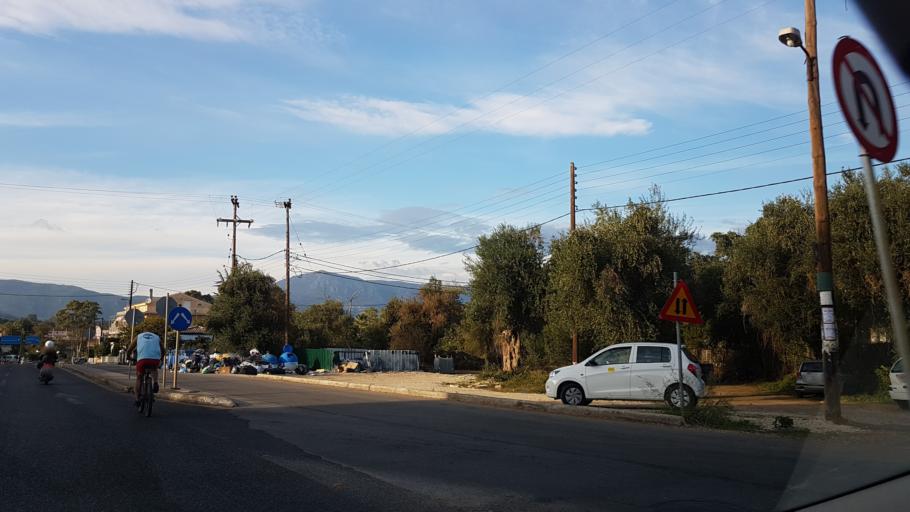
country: GR
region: Ionian Islands
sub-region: Nomos Kerkyras
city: Kontokali
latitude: 39.6566
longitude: 19.8397
